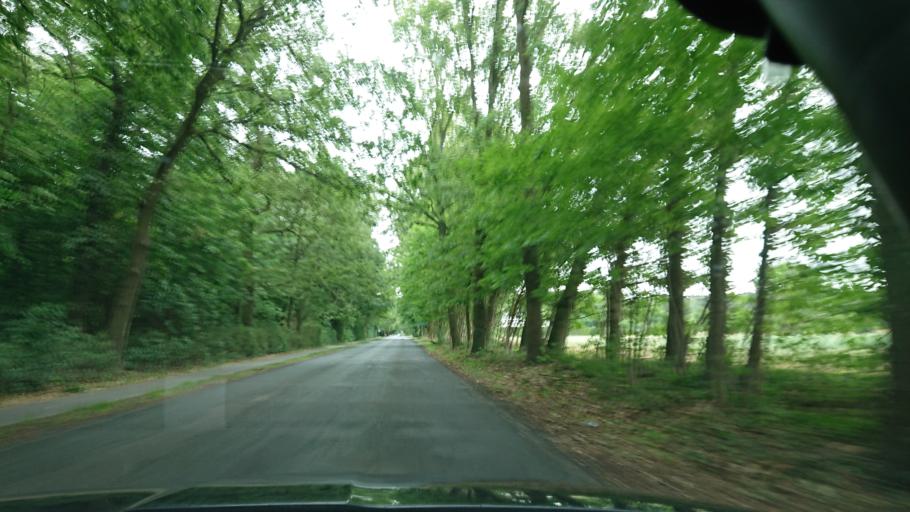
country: DE
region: Brandenburg
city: Kyritz
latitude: 52.9386
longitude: 12.4225
